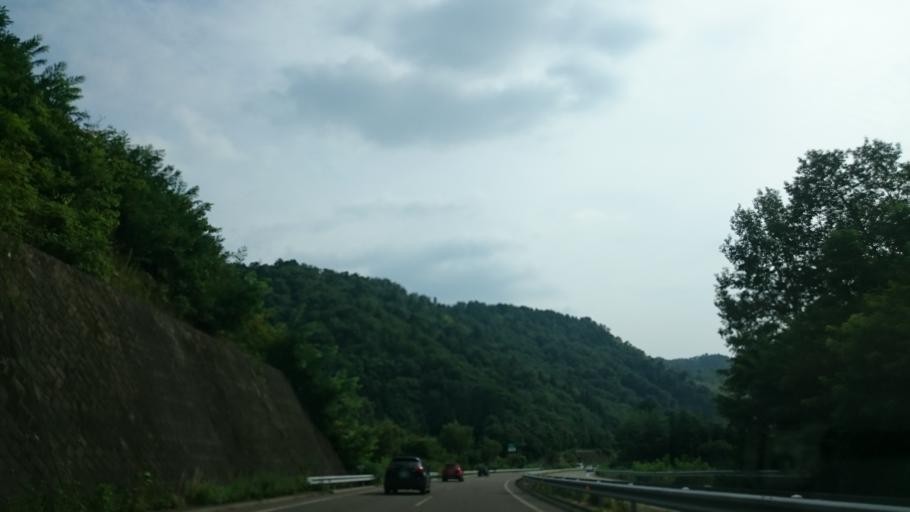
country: JP
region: Gifu
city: Mino
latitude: 35.5442
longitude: 136.9304
